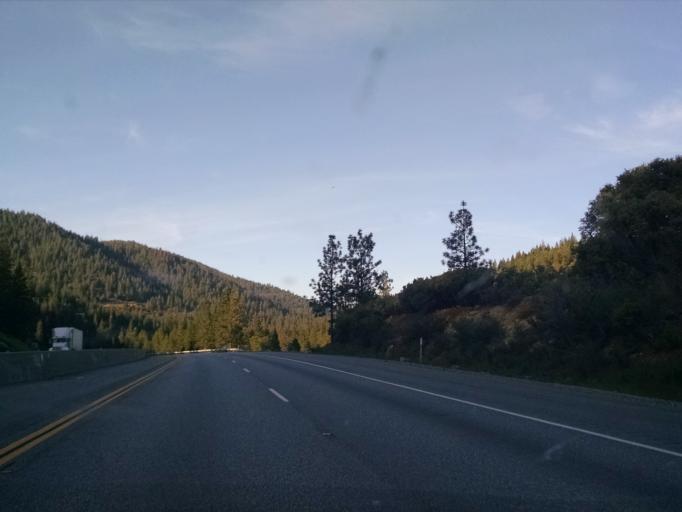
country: US
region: California
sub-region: Siskiyou County
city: Dunsmuir
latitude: 41.0358
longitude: -122.3963
